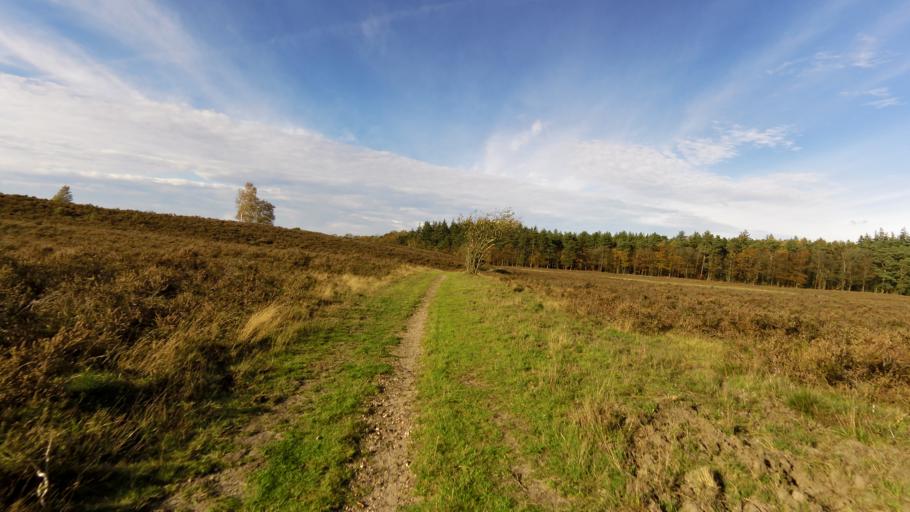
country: NL
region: Gelderland
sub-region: Gemeente Epe
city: Epe
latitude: 52.3816
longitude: 5.9968
